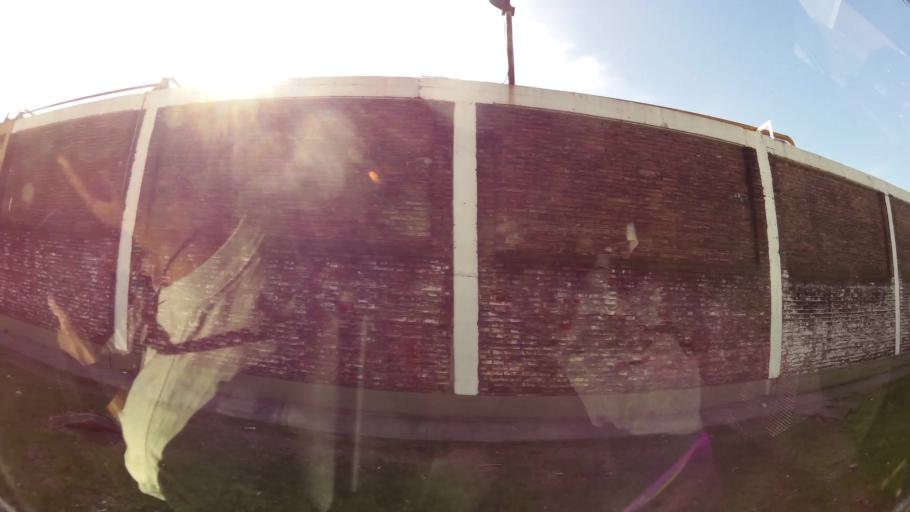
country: AR
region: Buenos Aires
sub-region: Partido de Quilmes
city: Quilmes
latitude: -34.8006
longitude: -58.2187
